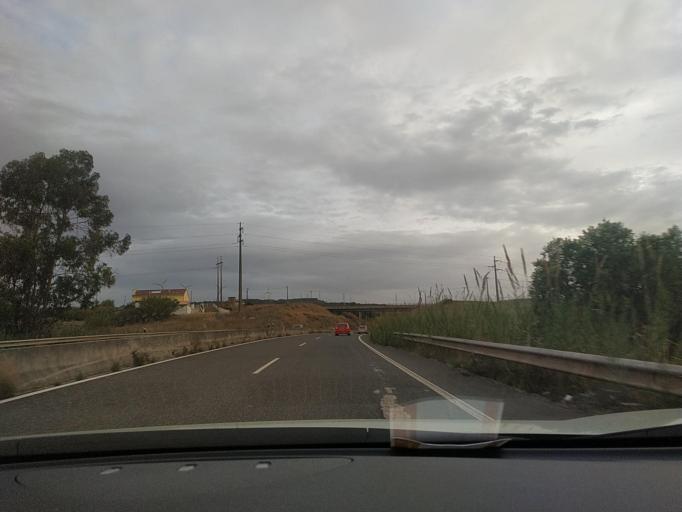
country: PT
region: Lisbon
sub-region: Loures
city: Santo Antao do Tojal
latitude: 38.8587
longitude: -9.1434
